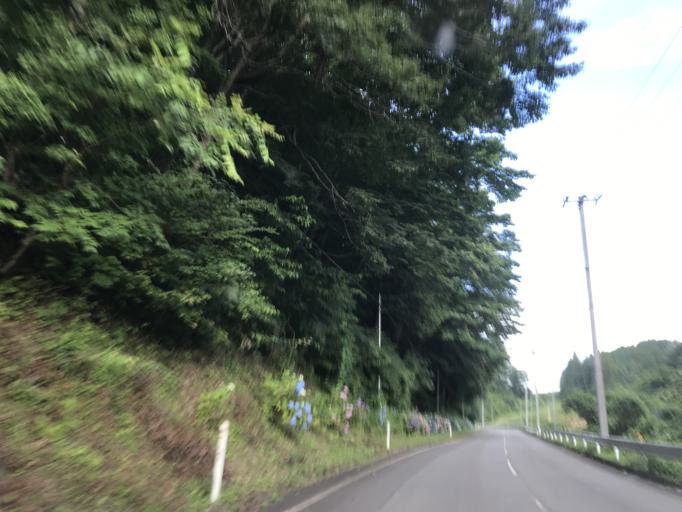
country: JP
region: Iwate
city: Ichinoseki
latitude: 38.9000
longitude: 140.9988
